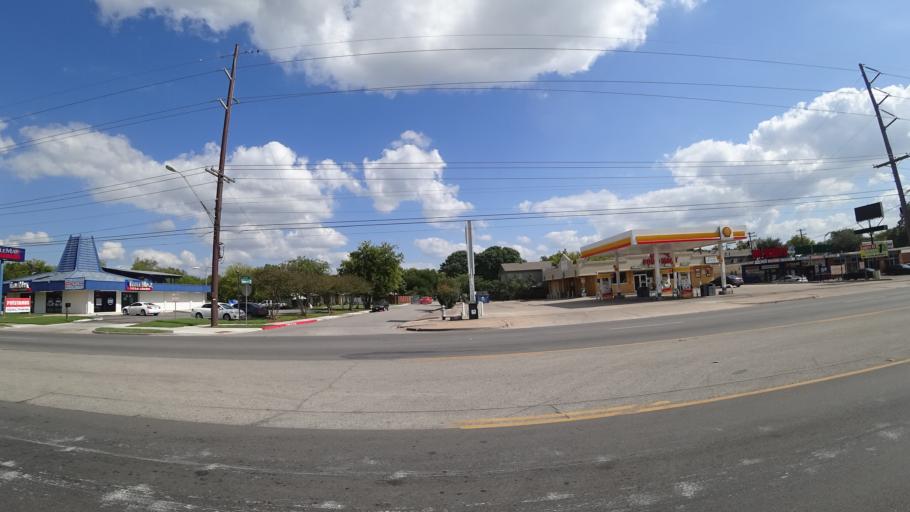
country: US
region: Texas
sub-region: Travis County
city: Wells Branch
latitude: 30.3582
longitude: -97.6999
